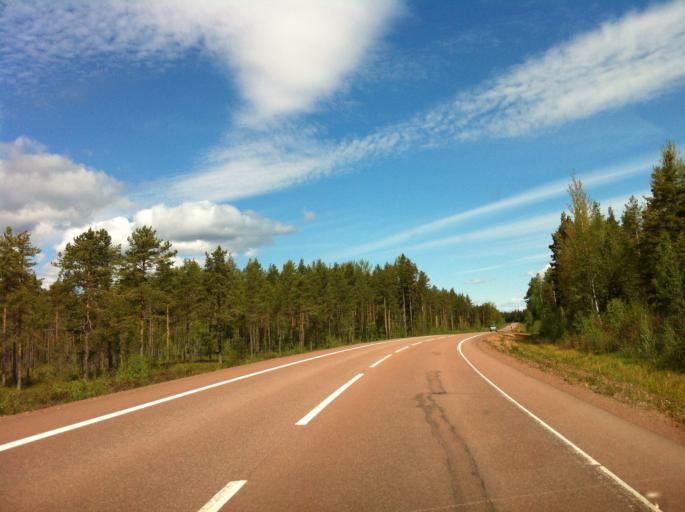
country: SE
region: Dalarna
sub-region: Mora Kommun
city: Mora
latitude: 60.9266
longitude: 14.5684
